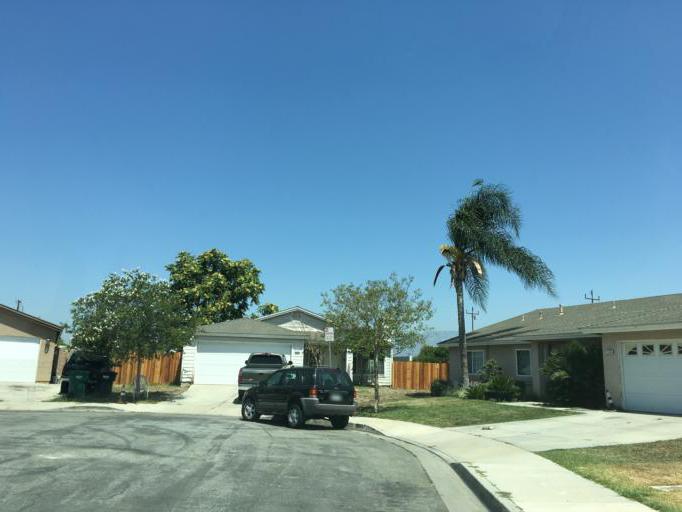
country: US
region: California
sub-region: Los Angeles County
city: Avocado Heights
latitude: 34.0471
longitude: -117.9941
